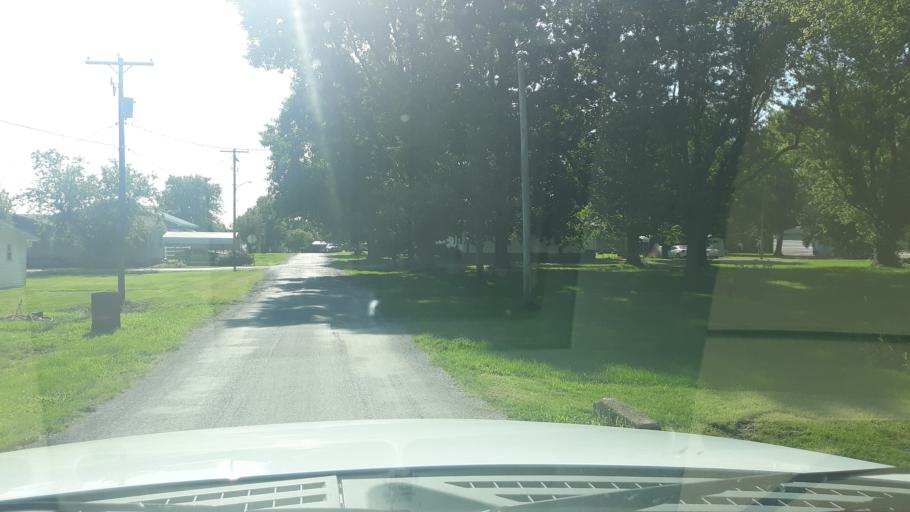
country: US
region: Illinois
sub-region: Saline County
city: Harrisburg
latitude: 37.8419
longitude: -88.6062
